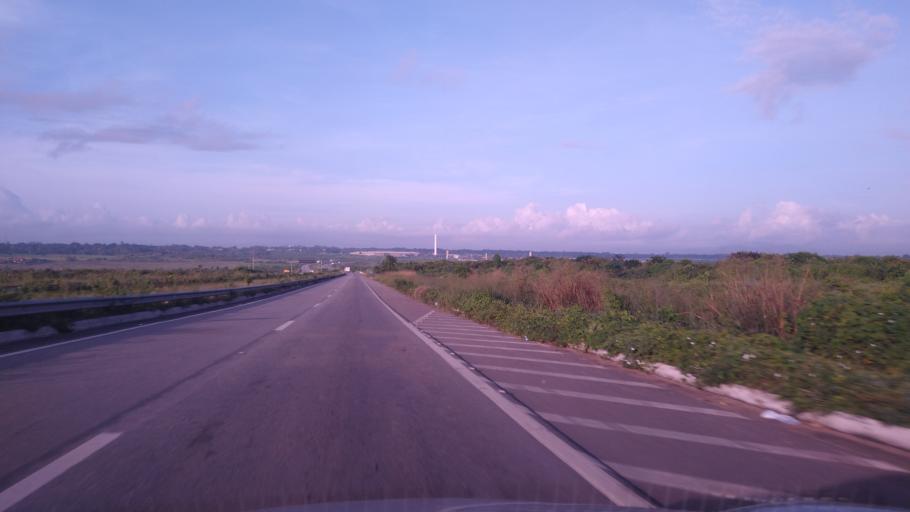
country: BR
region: Ceara
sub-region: Pacajus
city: Pacajus
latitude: -4.1520
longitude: -38.4798
